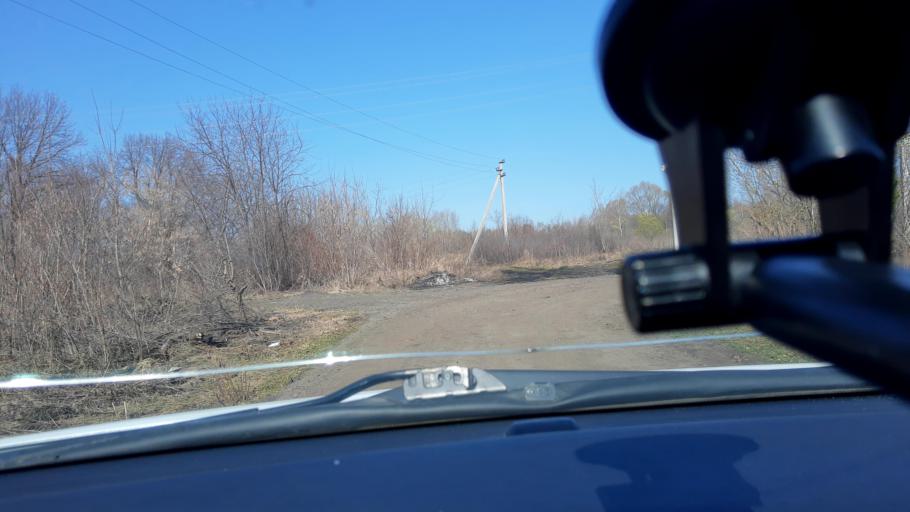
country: RU
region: Bashkortostan
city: Mikhaylovka
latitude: 54.7208
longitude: 55.8231
